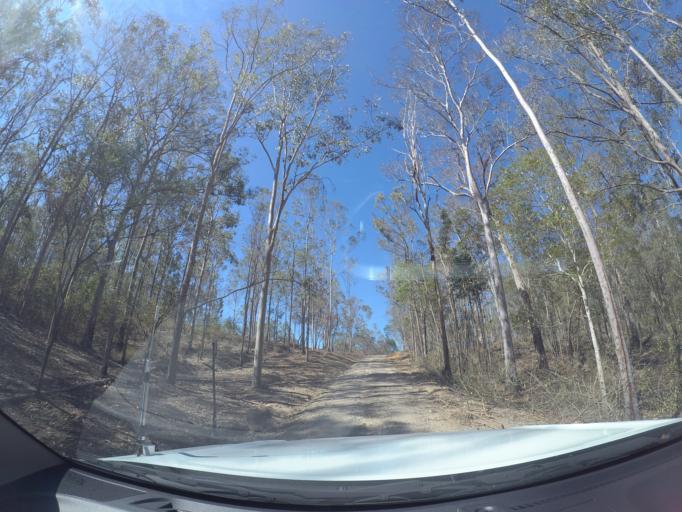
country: AU
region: Queensland
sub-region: Ipswich
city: Springfield Lakes
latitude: -27.7470
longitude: 152.9004
